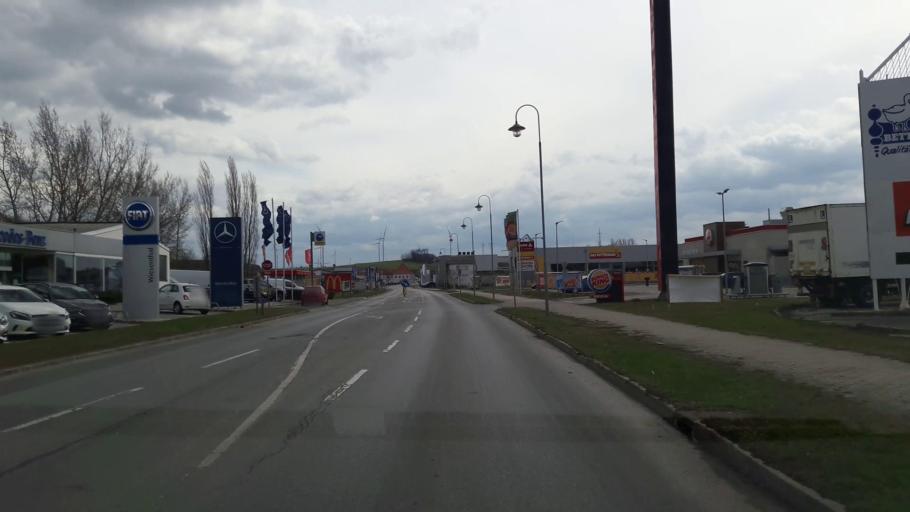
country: AT
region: Lower Austria
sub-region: Politischer Bezirk Mistelbach
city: Mistelbach
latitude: 48.5608
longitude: 16.5613
